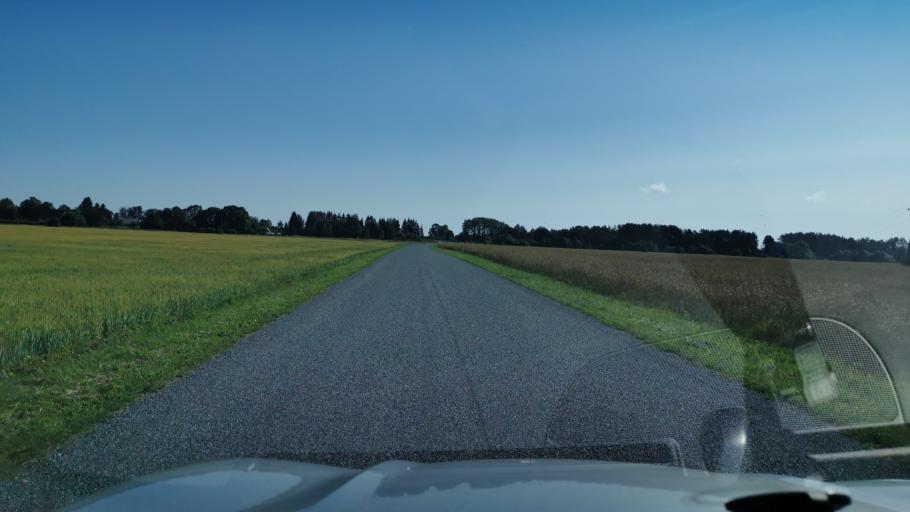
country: EE
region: Harju
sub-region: Paldiski linn
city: Paldiski
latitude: 59.2141
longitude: 24.0379
